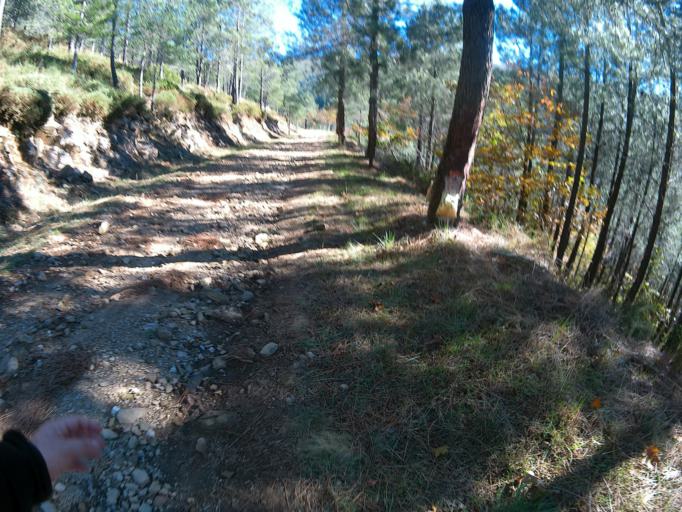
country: PT
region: Vila Real
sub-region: Mesao Frio
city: Mesao Frio
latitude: 41.2402
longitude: -7.9275
